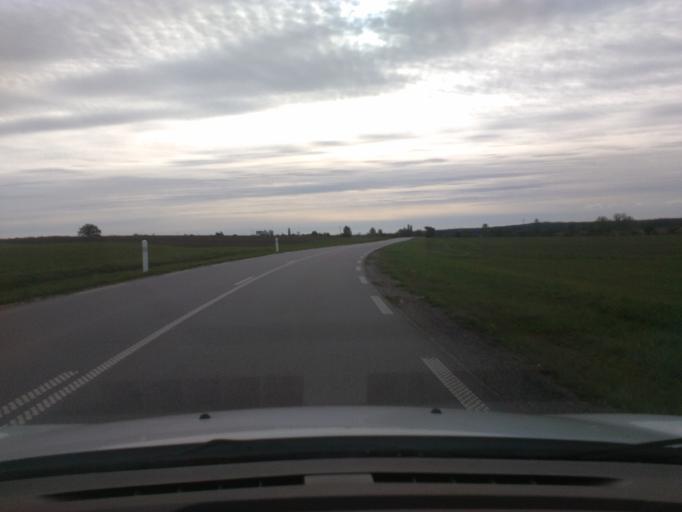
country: FR
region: Lorraine
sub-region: Departement des Vosges
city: Rambervillers
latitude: 48.3158
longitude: 6.6287
